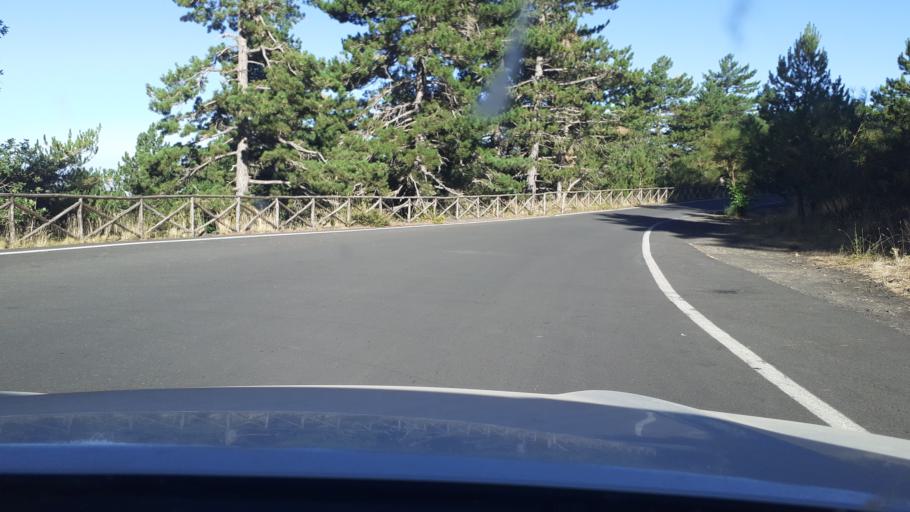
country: IT
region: Sicily
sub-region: Catania
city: Ragalna
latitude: 37.6900
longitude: 14.9736
